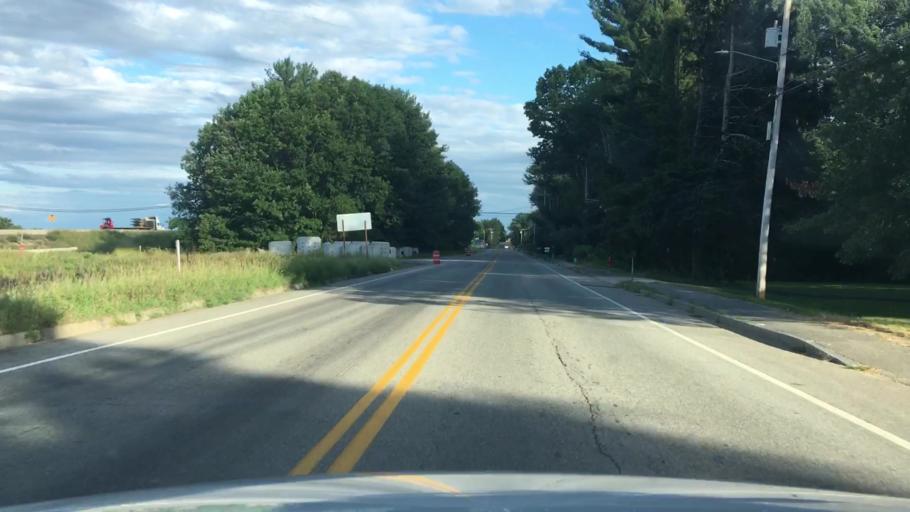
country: US
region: Maine
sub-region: York County
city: Eliot
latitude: 43.1268
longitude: -70.8396
